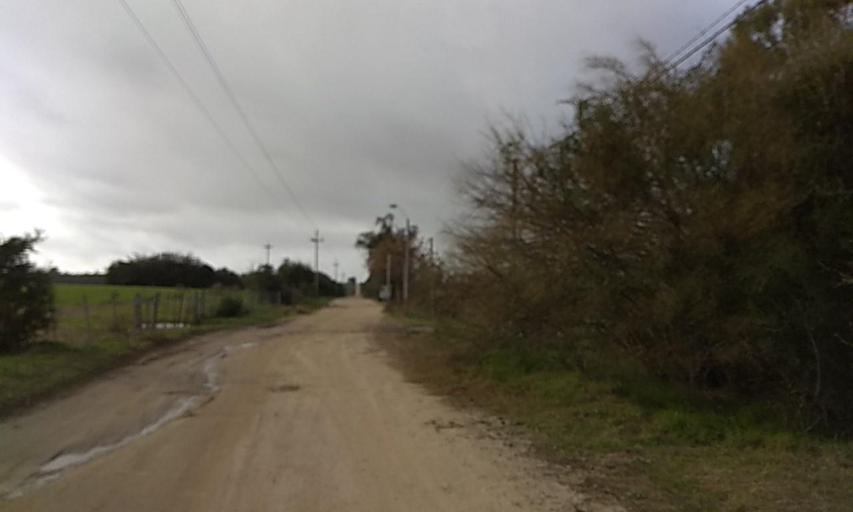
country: UY
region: Florida
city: Florida
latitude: -34.0578
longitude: -56.2214
